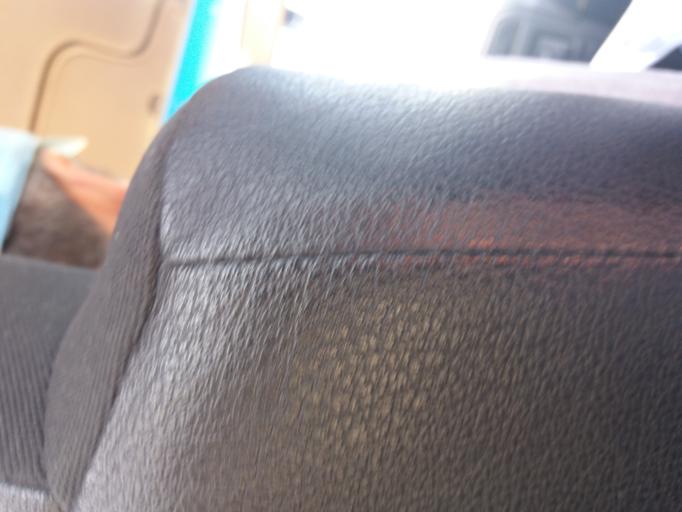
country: MX
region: Aguascalientes
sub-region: Aguascalientes
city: San Sebastian [Fraccionamiento]
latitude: 21.8115
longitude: -102.3063
